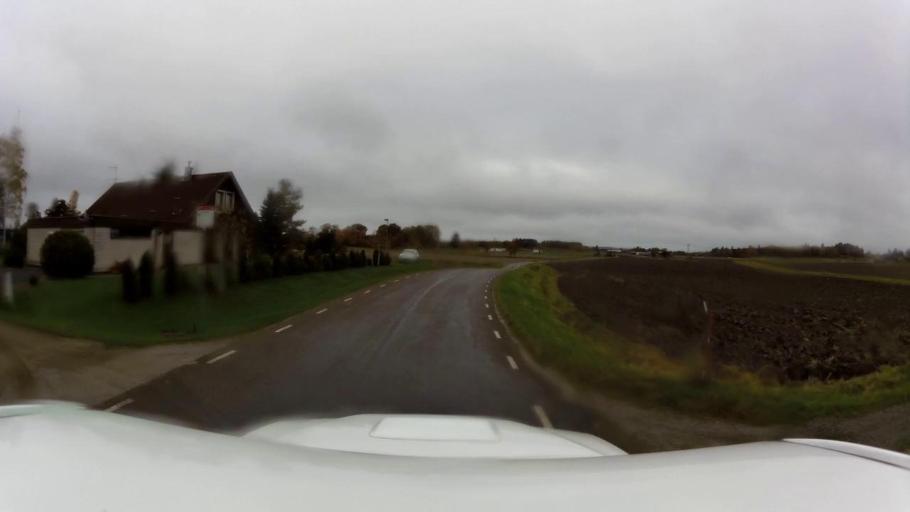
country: SE
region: OEstergoetland
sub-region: Linkopings Kommun
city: Linghem
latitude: 58.4676
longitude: 15.8243
